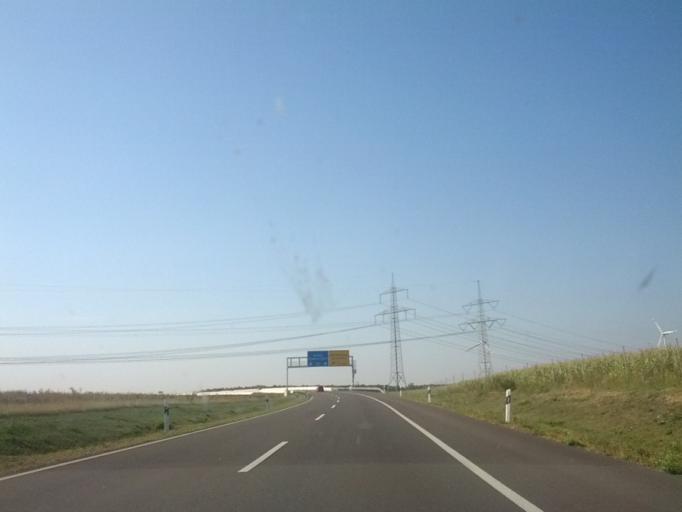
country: DE
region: Brandenburg
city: Ahrensfelde
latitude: 52.6220
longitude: 13.5625
